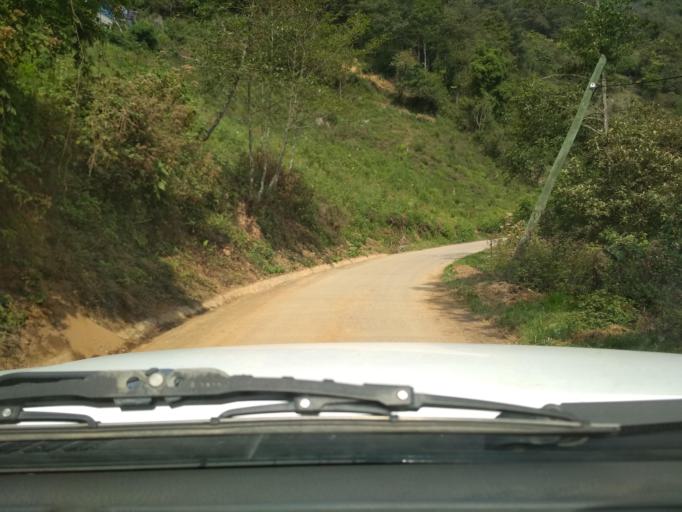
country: MX
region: Veracruz
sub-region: Camerino Z. Mendoza
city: Necoxtla
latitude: 18.7662
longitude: -97.1531
